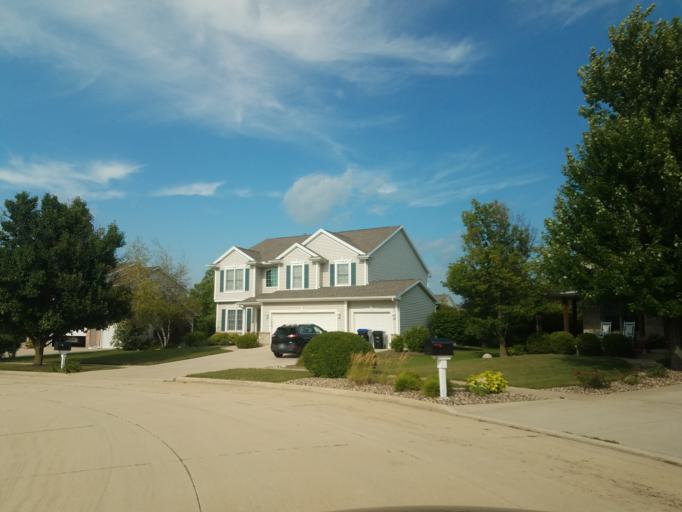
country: US
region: Illinois
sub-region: McLean County
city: Normal
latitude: 40.4984
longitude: -88.9172
